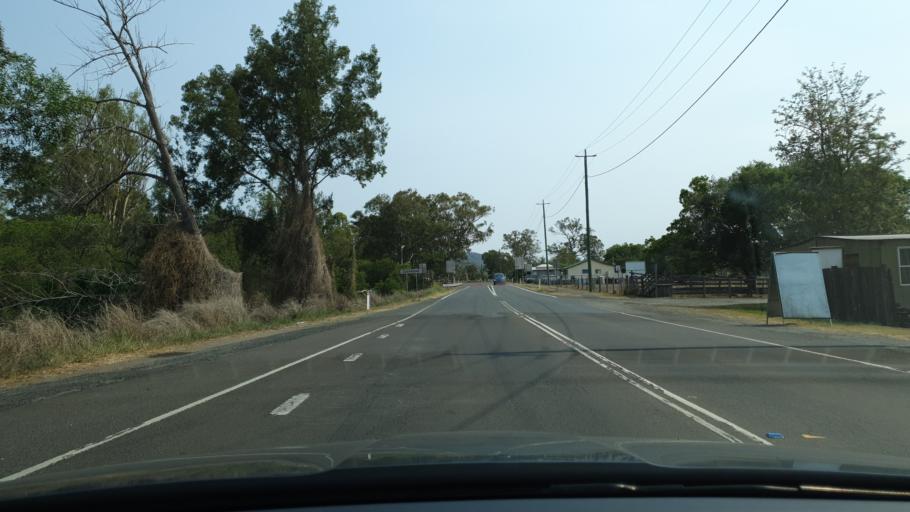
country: AU
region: Queensland
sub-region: Ipswich
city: Deebing Heights
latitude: -28.0045
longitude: 152.6810
